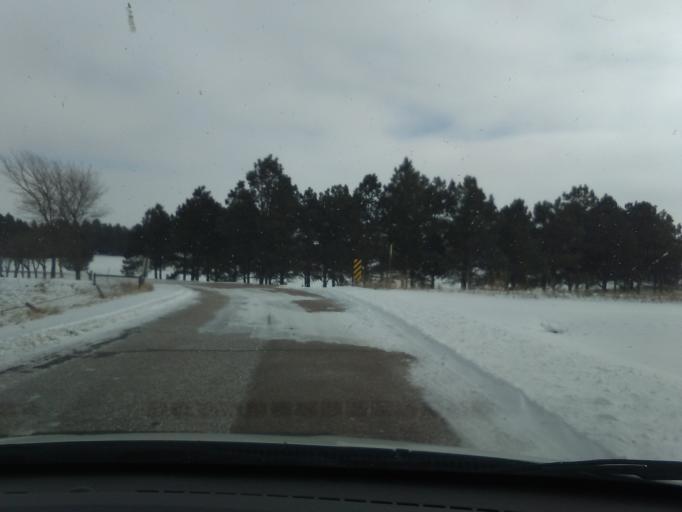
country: US
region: Nebraska
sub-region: Kimball County
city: Kimball
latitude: 41.2262
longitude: -103.6199
